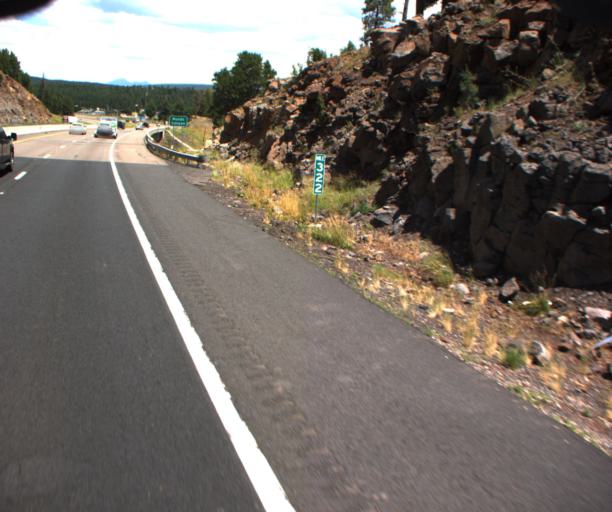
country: US
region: Arizona
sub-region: Coconino County
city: Sedona
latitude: 34.9319
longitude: -111.6492
